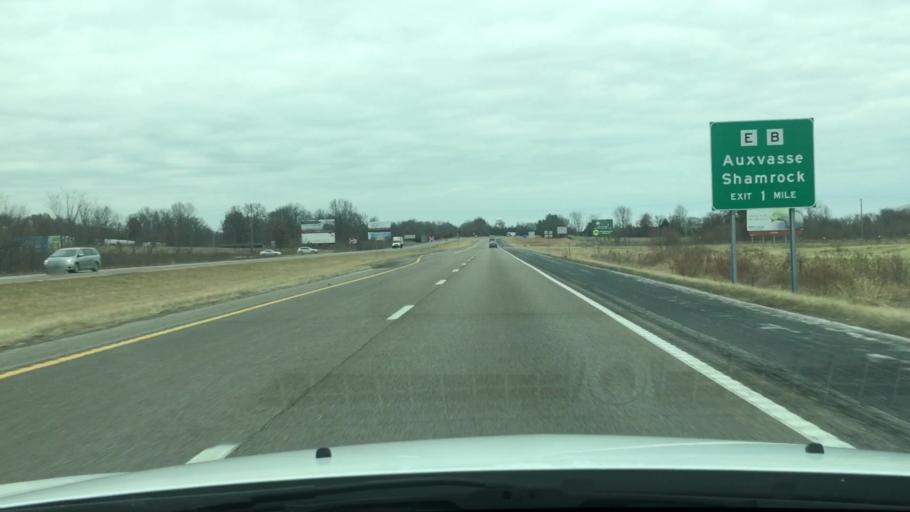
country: US
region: Missouri
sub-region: Callaway County
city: Fulton
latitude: 39.0017
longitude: -91.8929
